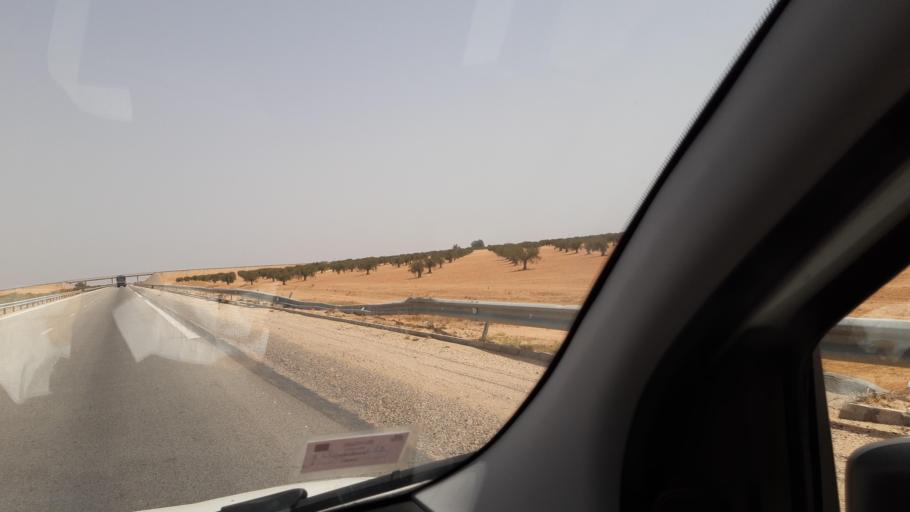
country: TN
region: Safaqis
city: Bi'r `Ali Bin Khalifah
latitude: 34.5292
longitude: 10.1156
